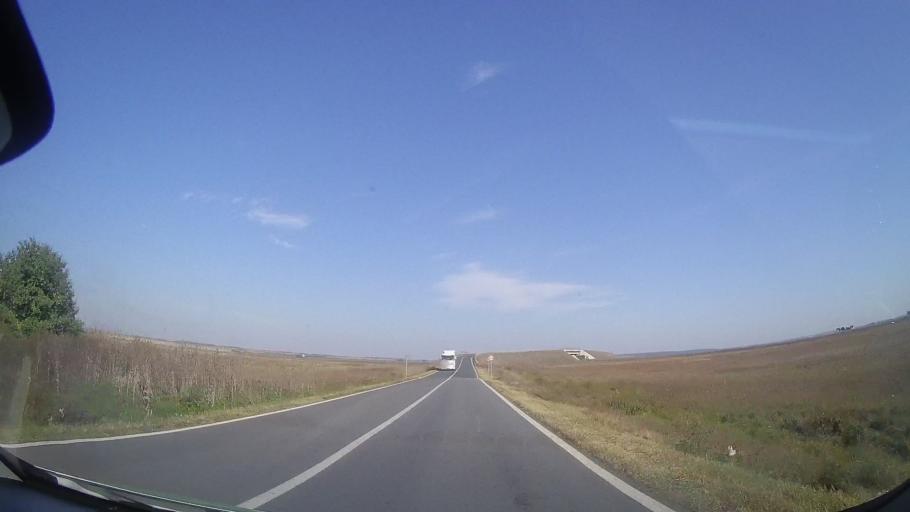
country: RO
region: Timis
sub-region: Comuna Belint
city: Belint
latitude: 45.7768
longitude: 21.7316
